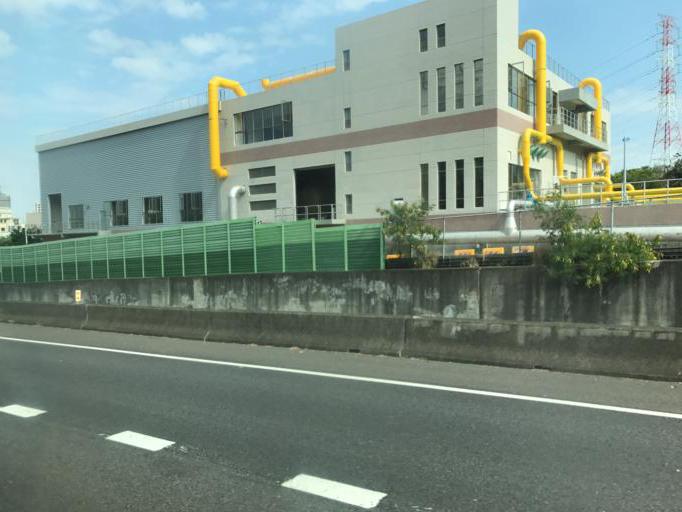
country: TW
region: Taiwan
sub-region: Hsinchu
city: Hsinchu
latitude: 24.7854
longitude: 121.0040
